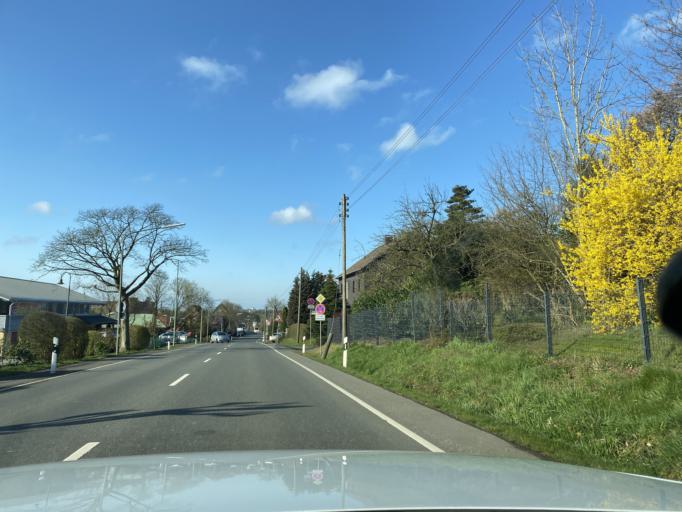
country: DE
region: North Rhine-Westphalia
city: Wermelskirchen
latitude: 51.1110
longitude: 7.1751
